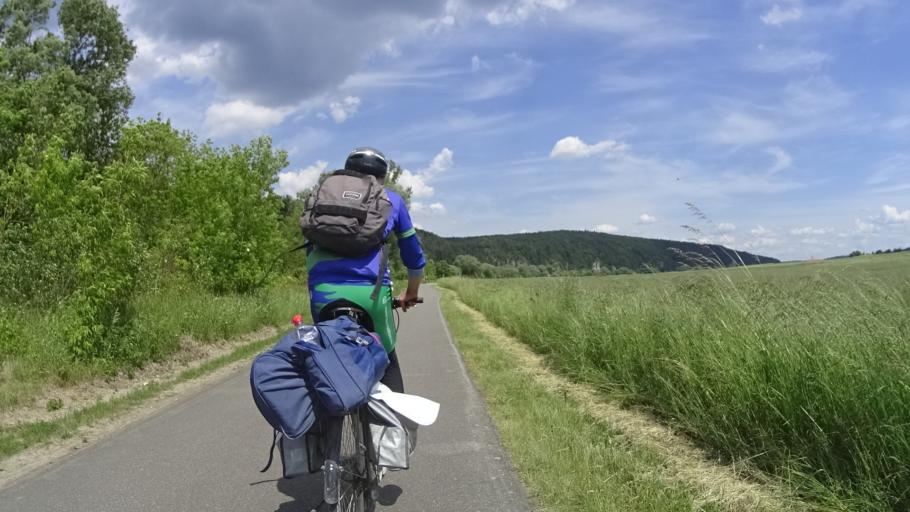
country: DE
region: Bavaria
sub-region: Lower Bavaria
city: Bad Abbach
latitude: 48.9563
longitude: 11.9885
